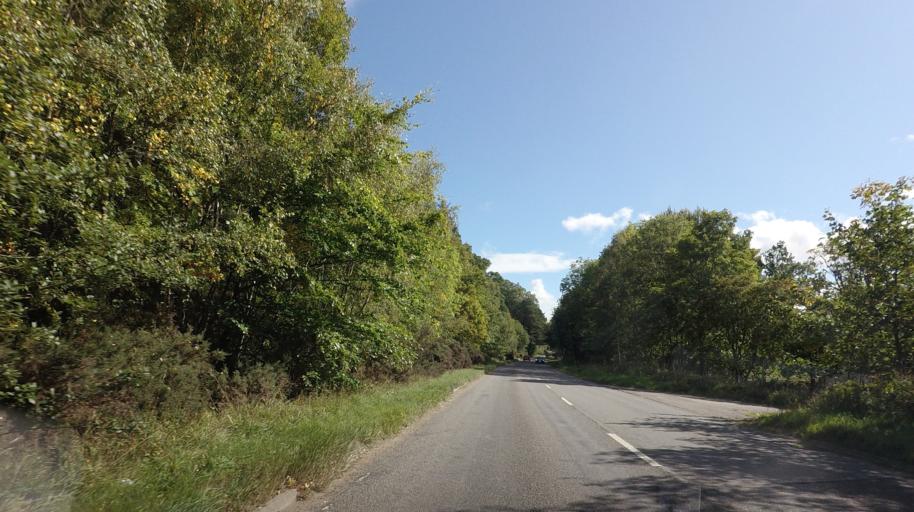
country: GB
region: Scotland
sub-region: Aberdeenshire
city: Banchory
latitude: 57.0587
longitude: -2.4567
